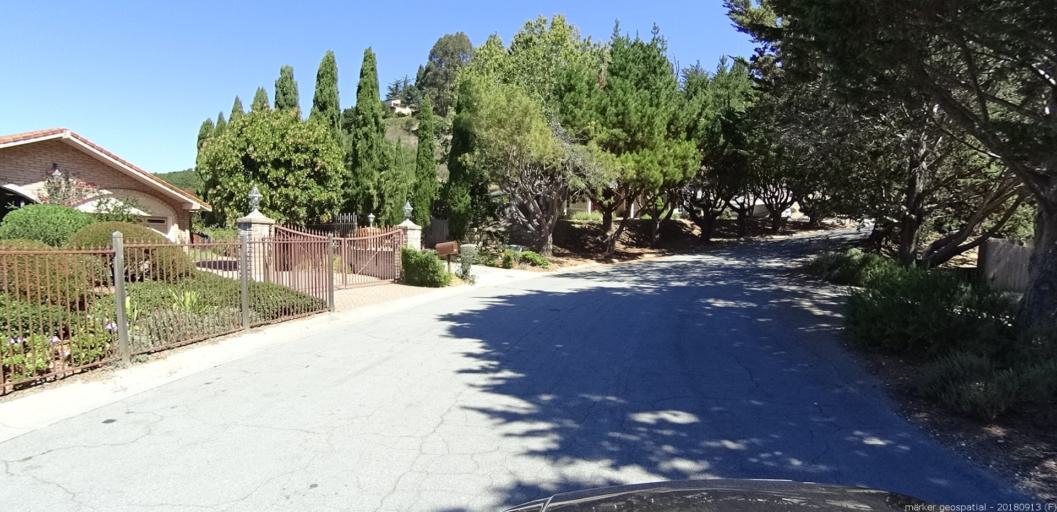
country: US
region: California
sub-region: Monterey County
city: Carmel Valley Village
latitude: 36.5428
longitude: -121.7980
